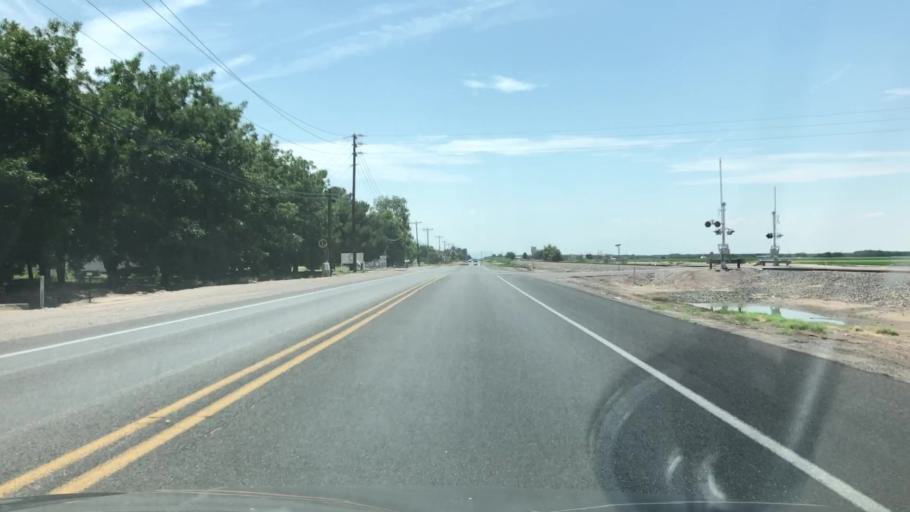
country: US
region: New Mexico
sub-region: Dona Ana County
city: University Park
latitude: 32.2488
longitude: -106.7499
